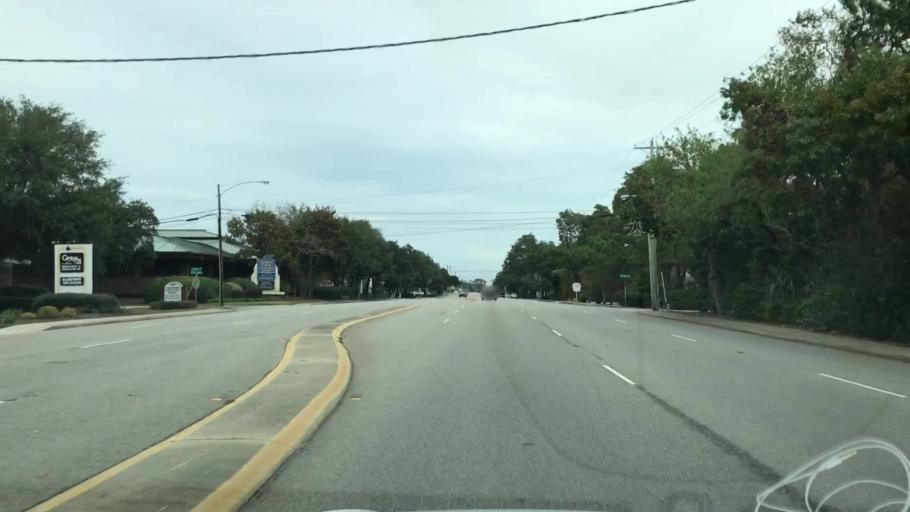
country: US
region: South Carolina
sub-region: Horry County
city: Myrtle Beach
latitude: 33.7129
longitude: -78.8594
